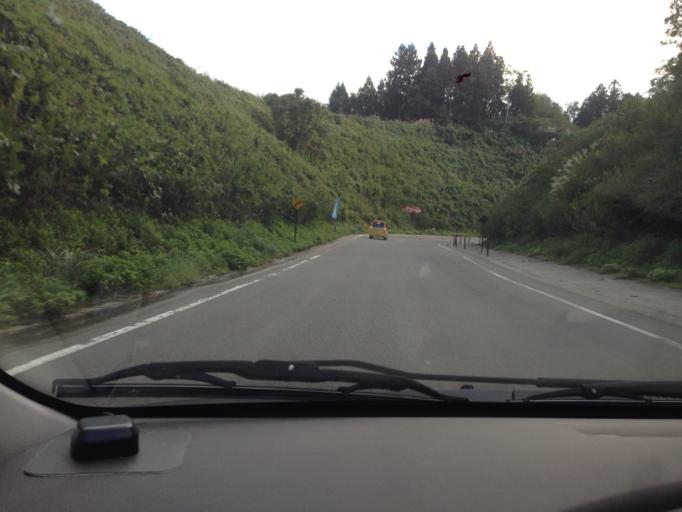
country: JP
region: Fukushima
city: Kitakata
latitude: 37.5772
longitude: 139.7708
